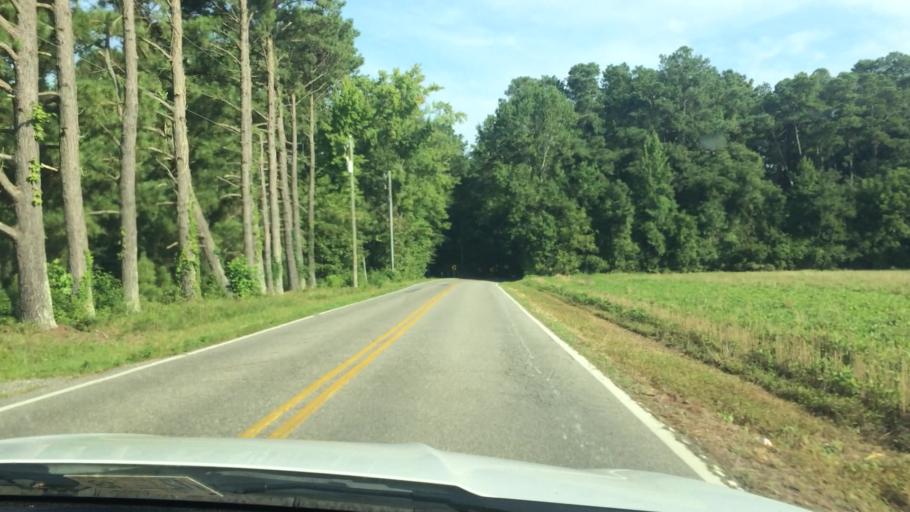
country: US
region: Virginia
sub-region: Middlesex County
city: Deltaville
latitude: 37.5851
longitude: -76.4524
